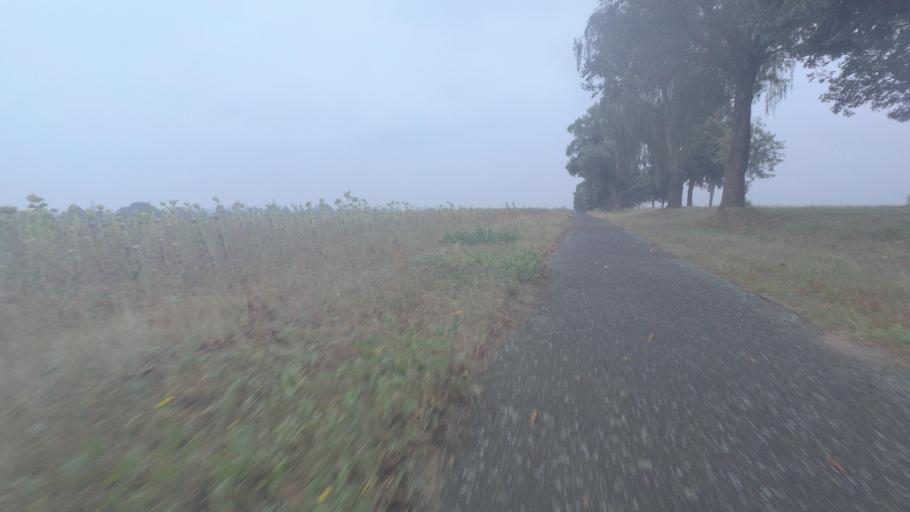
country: DE
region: Brandenburg
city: Heiligengrabe
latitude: 53.1273
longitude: 12.3756
